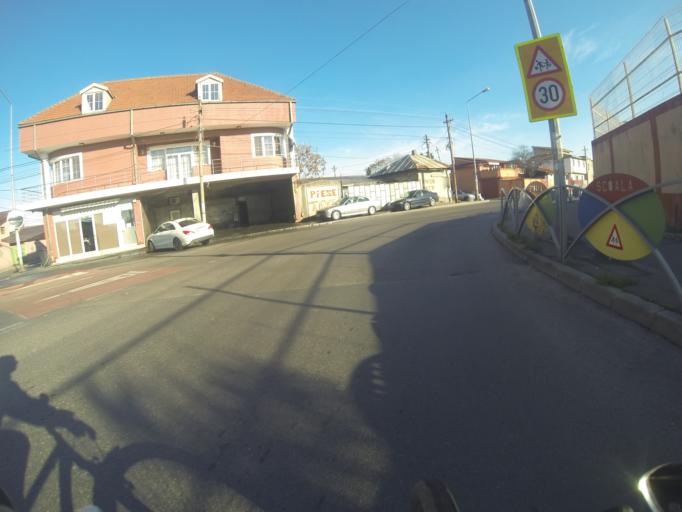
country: RO
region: Bucuresti
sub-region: Municipiul Bucuresti
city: Bucuresti
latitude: 44.4003
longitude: 26.0778
